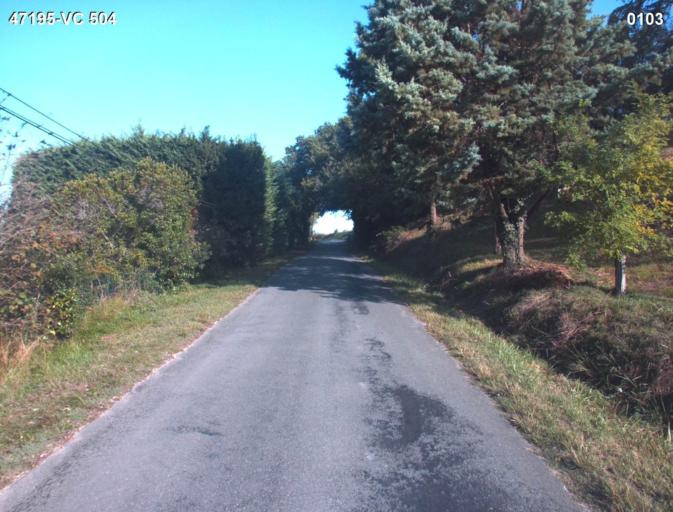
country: FR
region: Aquitaine
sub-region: Departement du Lot-et-Garonne
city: Nerac
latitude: 44.1491
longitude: 0.3369
